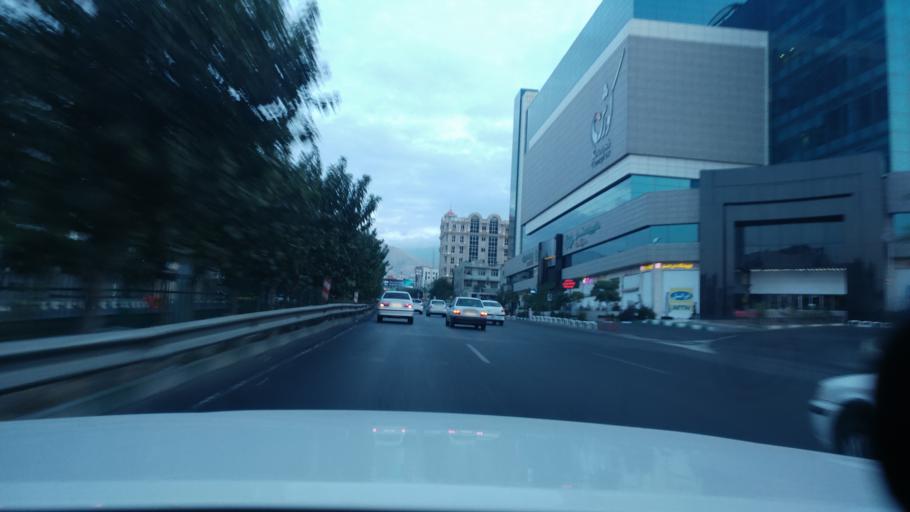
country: IR
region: Tehran
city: Tehran
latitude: 35.7370
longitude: 51.3127
